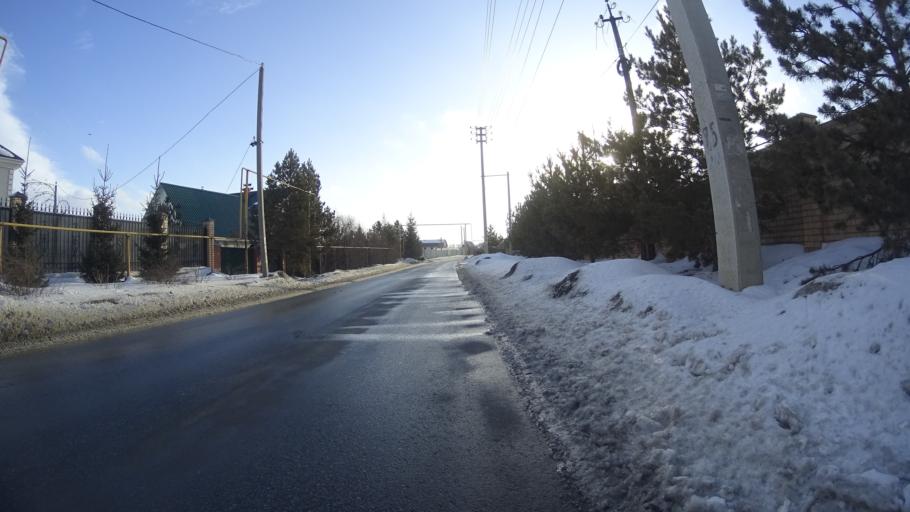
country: RU
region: Chelyabinsk
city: Sargazy
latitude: 55.1116
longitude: 61.2795
